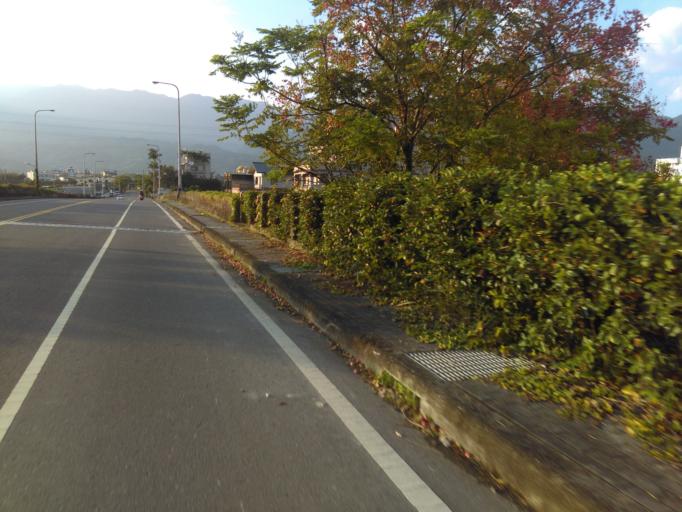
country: TW
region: Taiwan
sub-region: Yilan
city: Yilan
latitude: 24.8063
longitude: 121.7724
